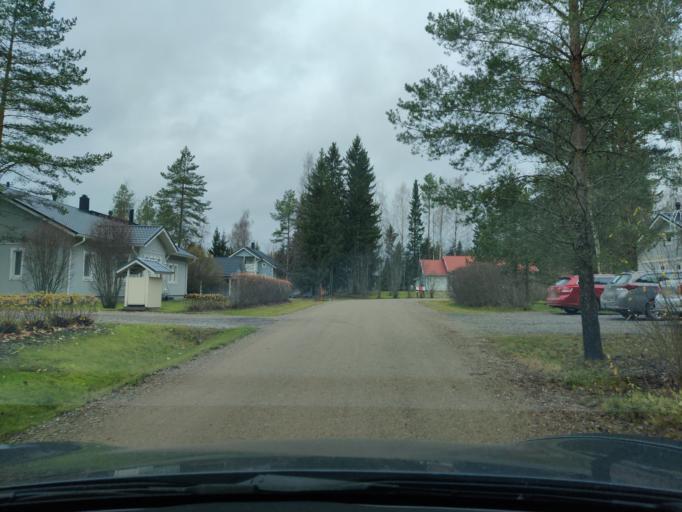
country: FI
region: Northern Savo
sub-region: Ylae-Savo
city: Kiuruvesi
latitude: 63.6413
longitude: 26.6380
